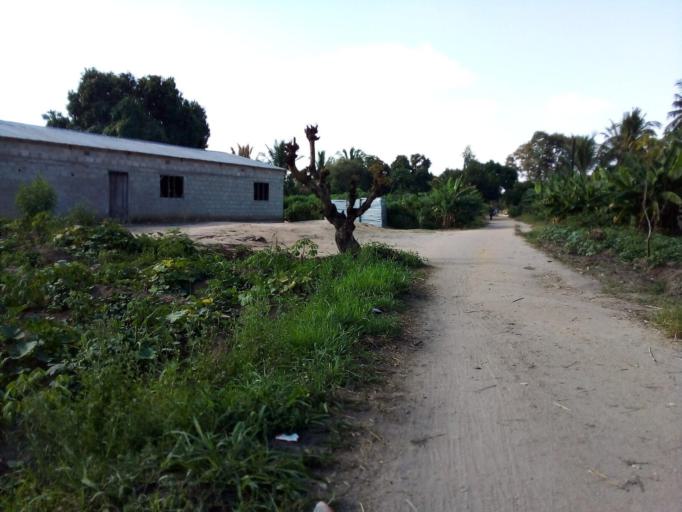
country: MZ
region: Zambezia
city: Quelimane
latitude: -17.6028
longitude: 36.8223
